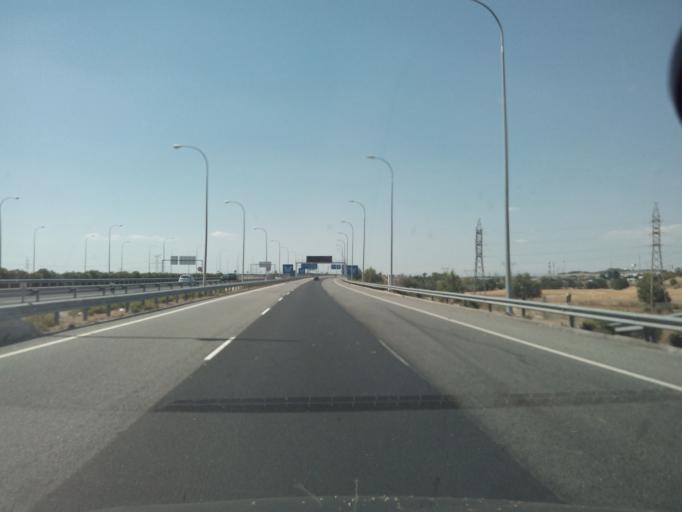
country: ES
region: Madrid
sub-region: Provincia de Madrid
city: San Fernando de Henares
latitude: 40.4393
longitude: -3.5101
